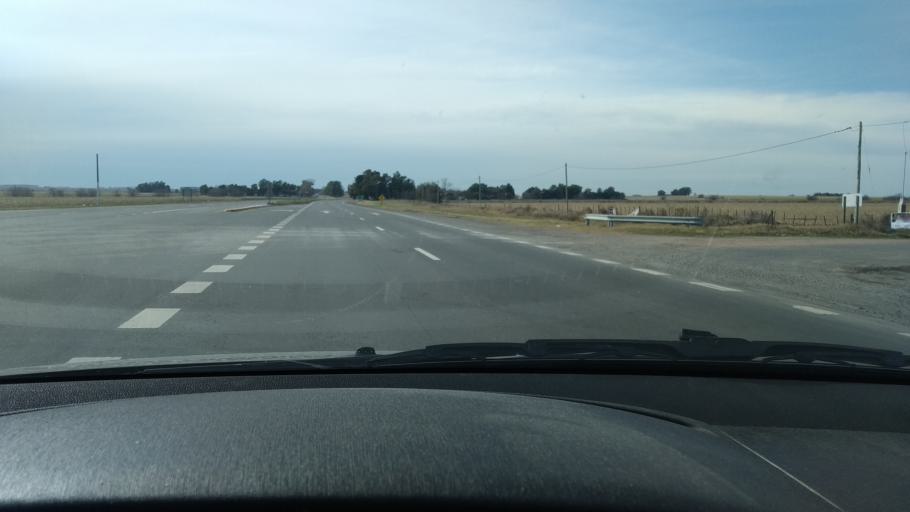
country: AR
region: Buenos Aires
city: Olavarria
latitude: -36.8776
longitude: -60.1431
